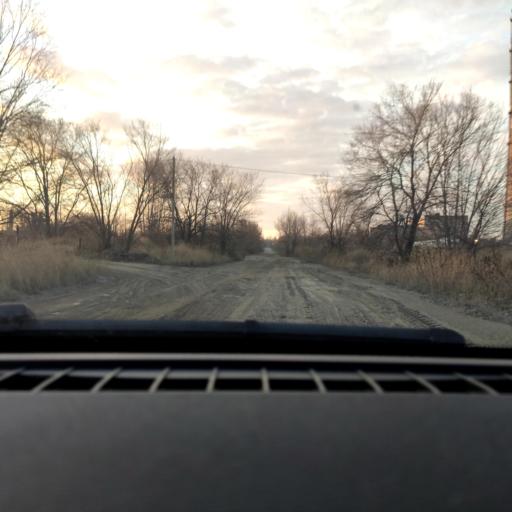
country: RU
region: Voronezj
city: Maslovka
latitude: 51.6111
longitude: 39.2670
